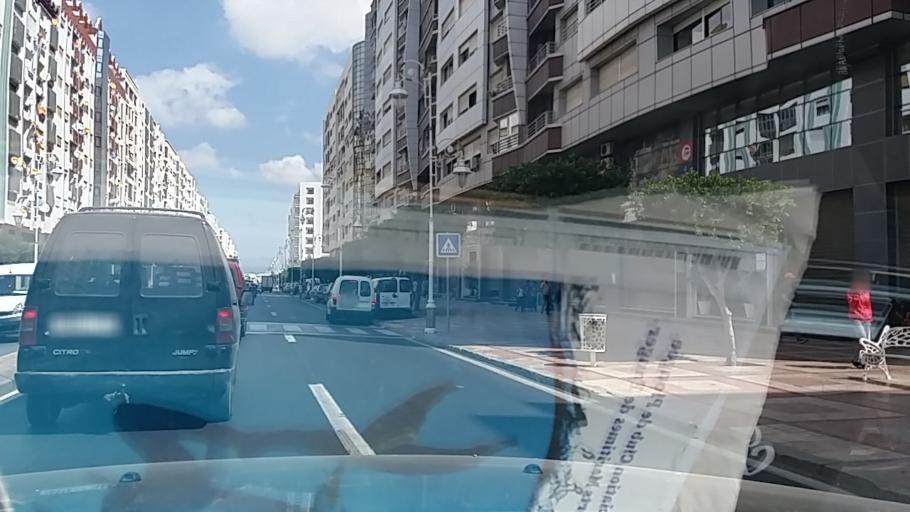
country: MA
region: Tanger-Tetouan
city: Tetouan
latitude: 35.5797
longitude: -5.3545
